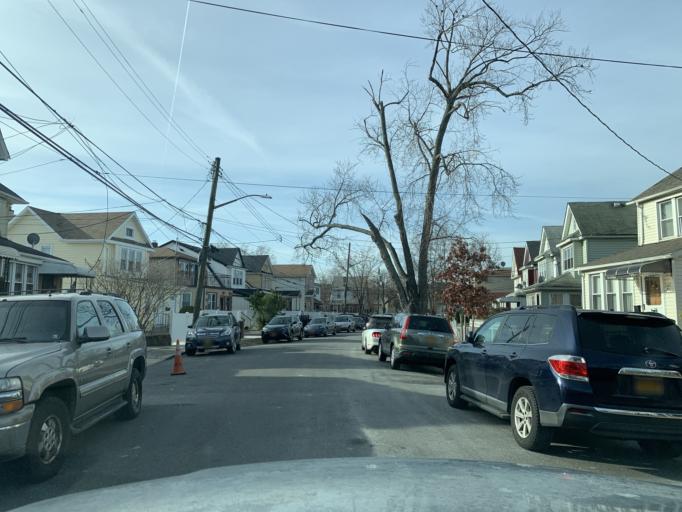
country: US
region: New York
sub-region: Queens County
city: Jamaica
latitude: 40.6960
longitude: -73.7847
